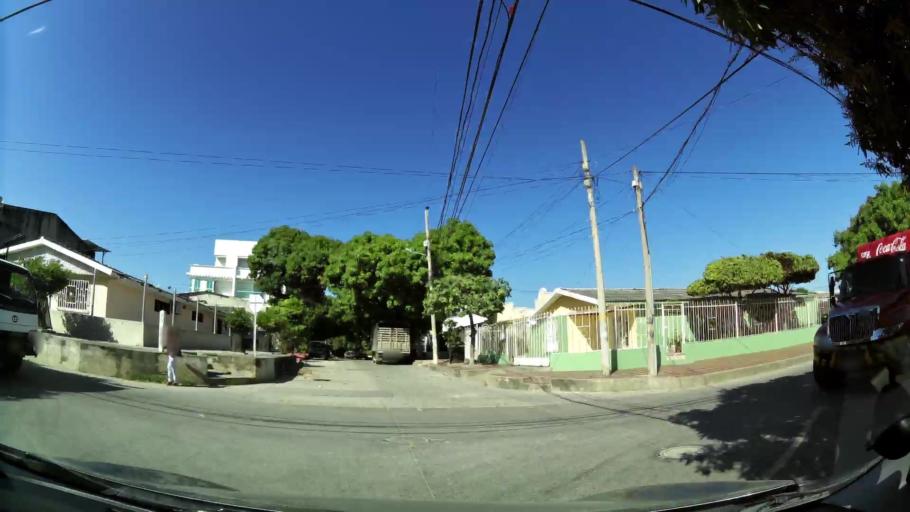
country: CO
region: Atlantico
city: Barranquilla
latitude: 10.9576
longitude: -74.7885
